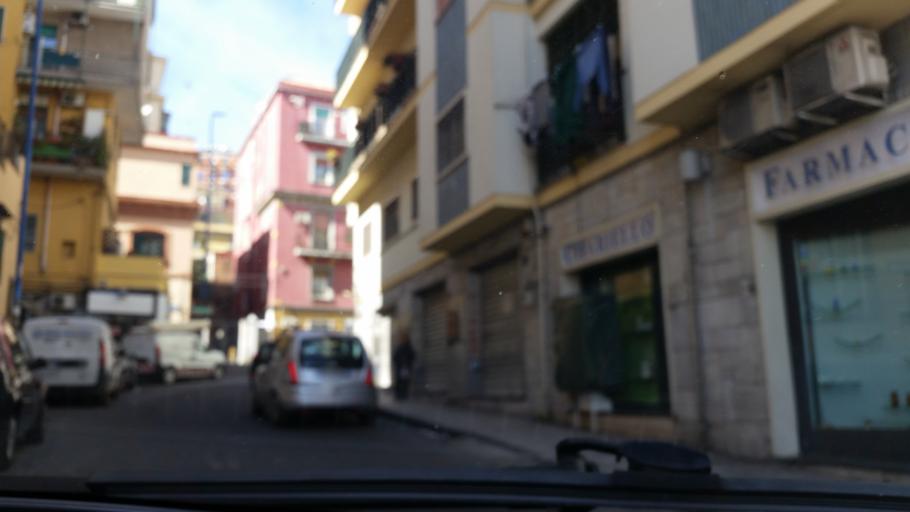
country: IT
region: Campania
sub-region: Provincia di Napoli
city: Napoli
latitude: 40.8541
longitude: 14.2340
